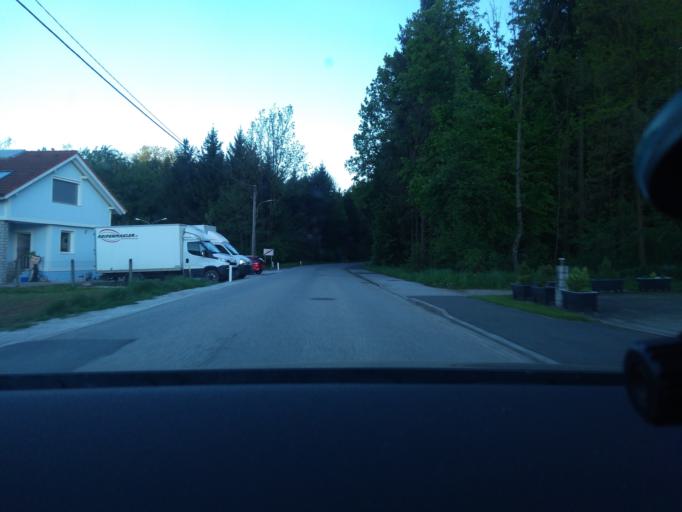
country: AT
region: Styria
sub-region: Politischer Bezirk Deutschlandsberg
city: Lannach
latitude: 46.9531
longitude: 15.3279
